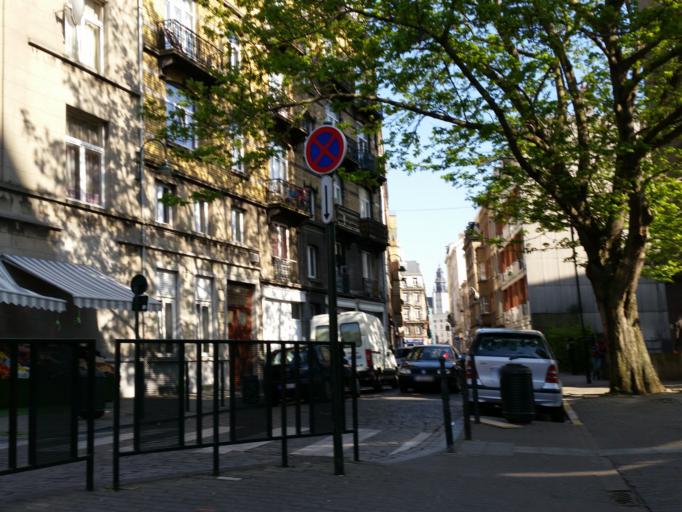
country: BE
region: Brussels Capital
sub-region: Bruxelles-Capitale
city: Brussels
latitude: 50.8452
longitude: 4.3437
